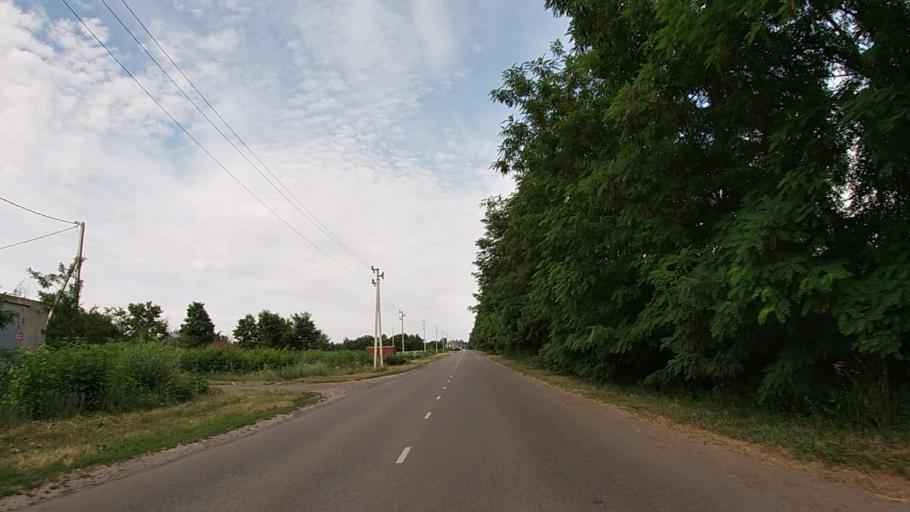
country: RU
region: Belgorod
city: Severnyy
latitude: 50.6932
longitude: 36.5674
